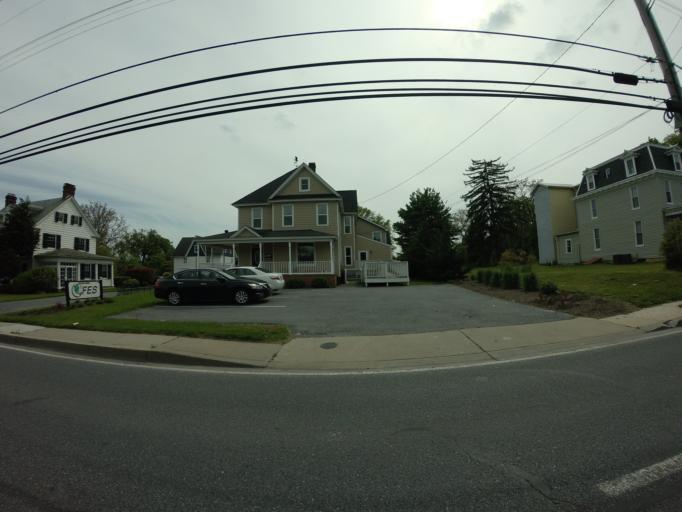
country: US
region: Maryland
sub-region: Baltimore County
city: Reisterstown
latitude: 39.4536
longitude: -76.8225
